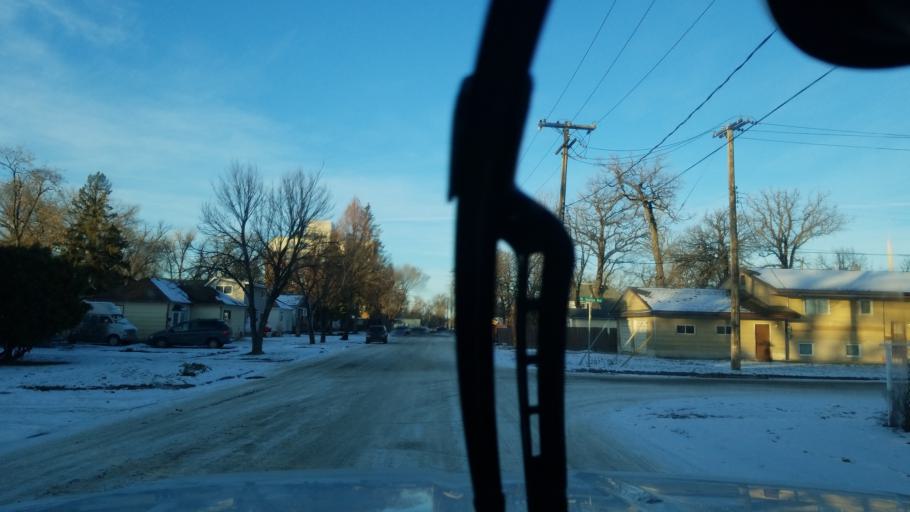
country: CA
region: Manitoba
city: Portage la Prairie
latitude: 49.9716
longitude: -98.3020
